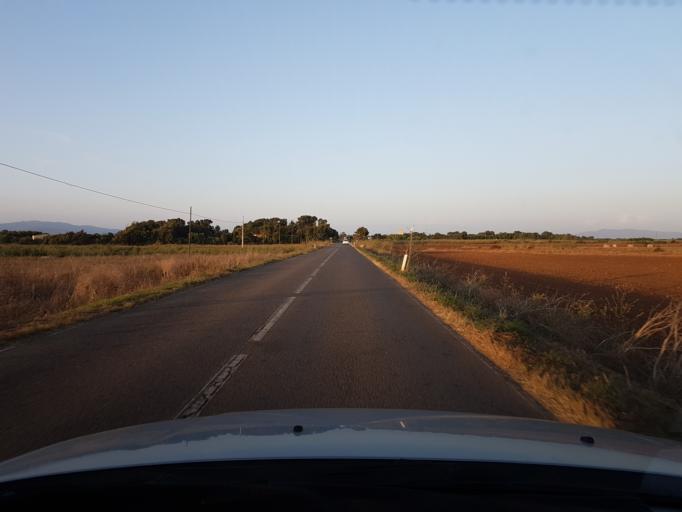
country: IT
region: Sardinia
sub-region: Provincia di Oristano
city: Cabras
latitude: 39.9132
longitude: 8.4452
